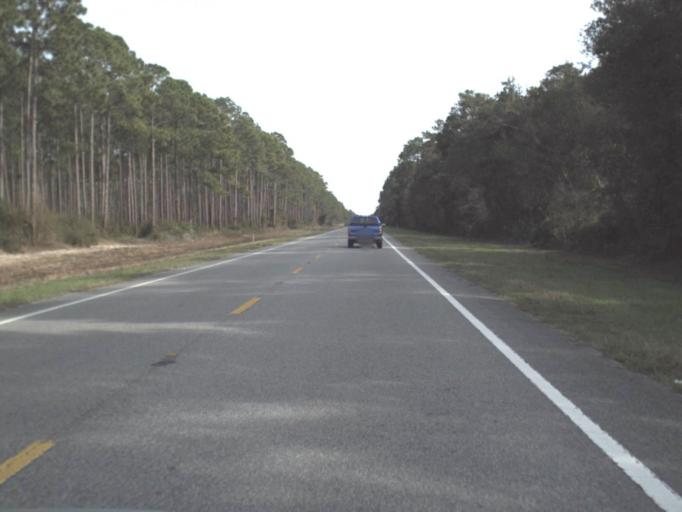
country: US
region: Florida
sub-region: Bay County
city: Mexico Beach
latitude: 29.9700
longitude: -85.4559
